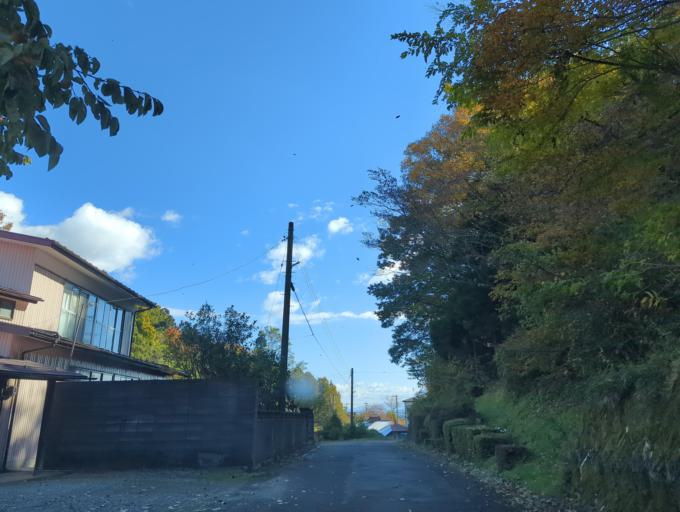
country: JP
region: Fukushima
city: Koriyama
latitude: 37.4571
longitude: 140.2989
